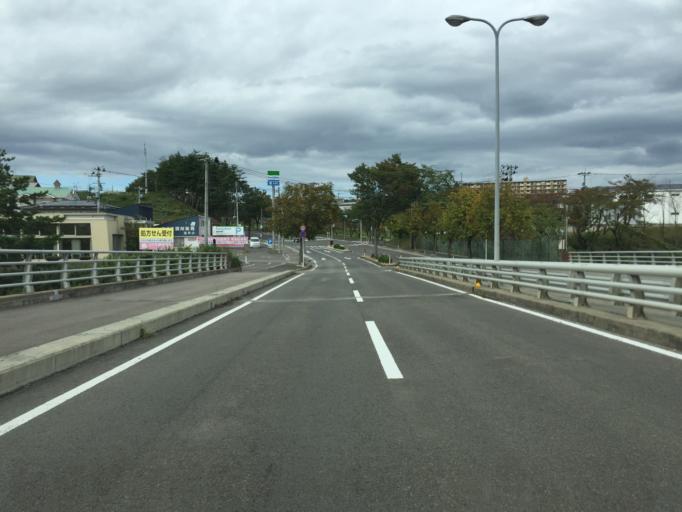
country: JP
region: Fukushima
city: Fukushima-shi
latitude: 37.6927
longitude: 140.4726
